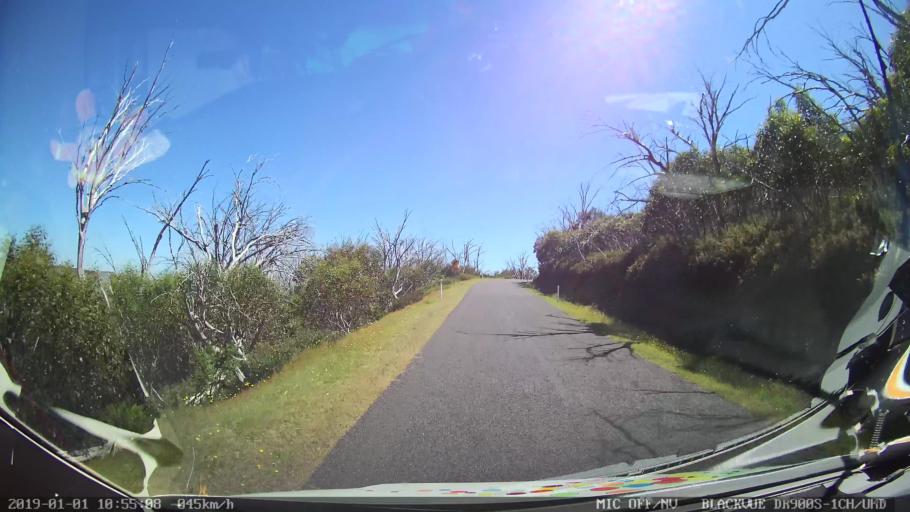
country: AU
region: New South Wales
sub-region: Snowy River
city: Jindabyne
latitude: -36.0096
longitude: 148.3875
